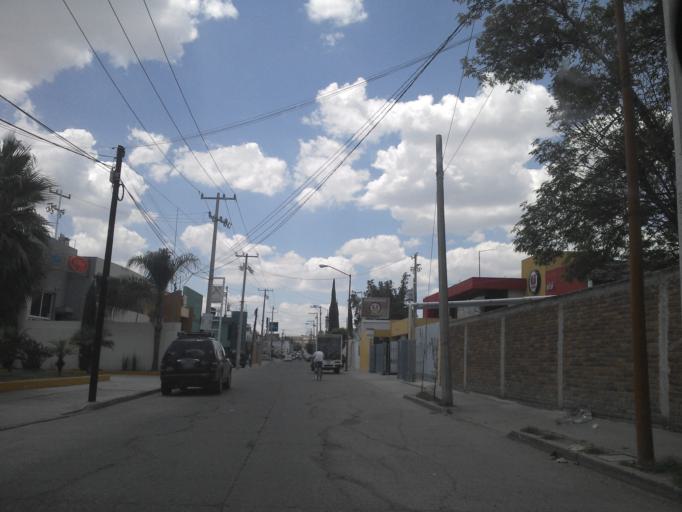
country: MX
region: Guanajuato
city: San Francisco del Rincon
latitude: 21.0262
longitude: -101.8576
